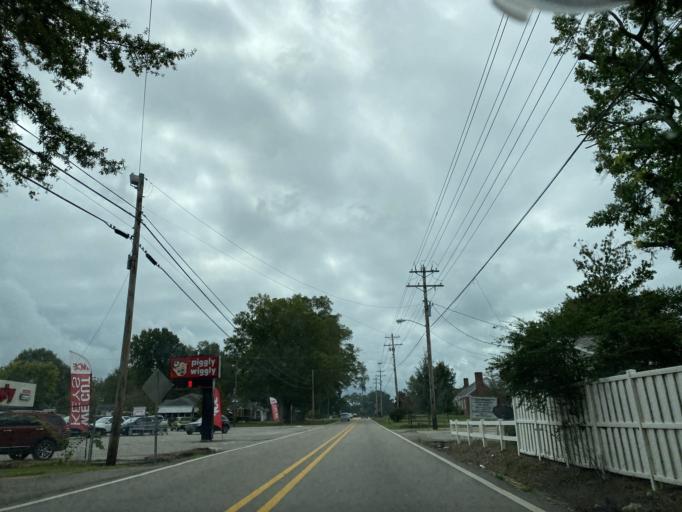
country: US
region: Mississippi
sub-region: Tishomingo County
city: Belmont
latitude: 34.5061
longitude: -88.2071
